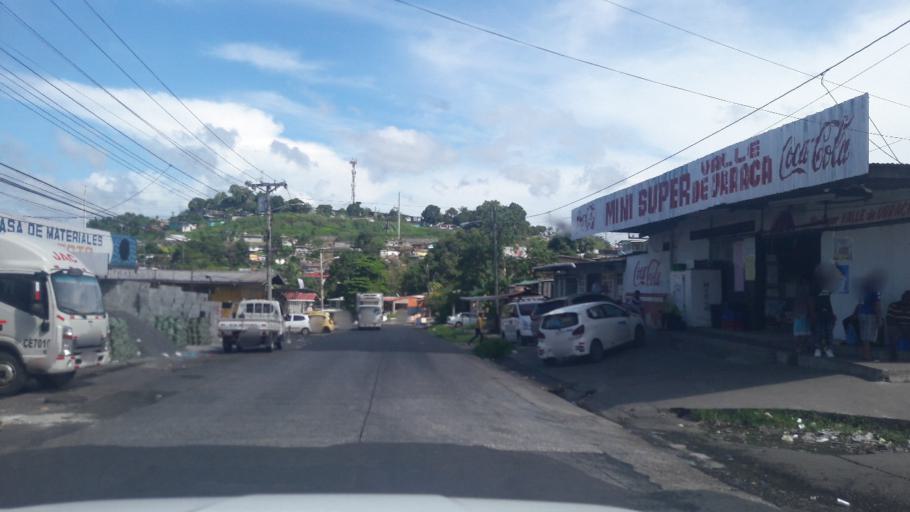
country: PA
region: Panama
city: San Miguelito
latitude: 9.0680
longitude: -79.4879
